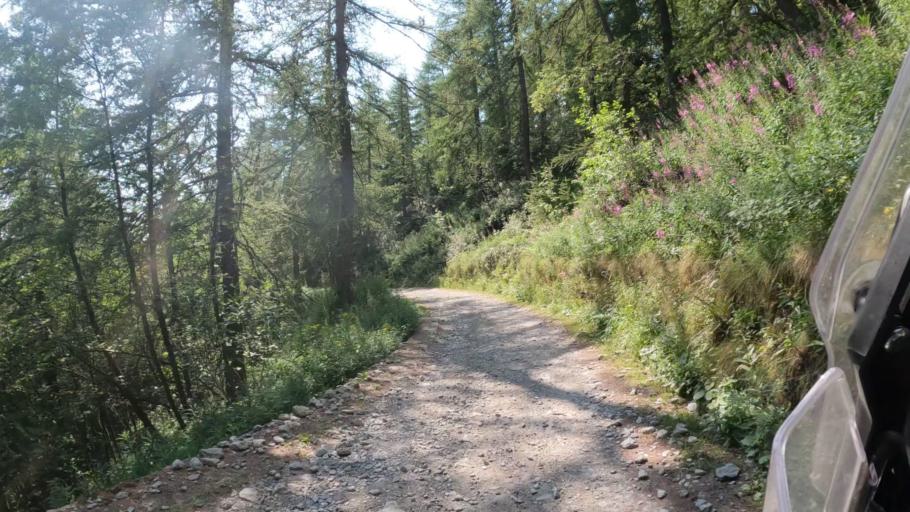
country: IT
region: Piedmont
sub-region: Provincia di Cuneo
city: Briga Alta
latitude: 44.0964
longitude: 7.7196
